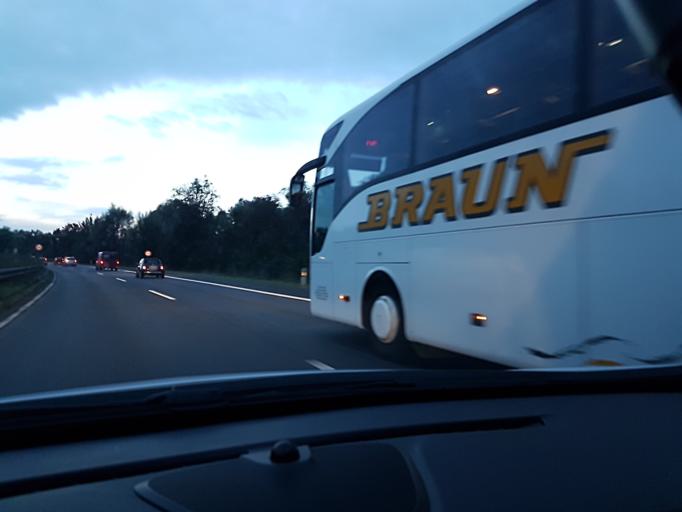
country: DE
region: Hesse
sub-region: Regierungsbezirk Darmstadt
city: Bad Homburg vor der Hoehe
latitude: 50.1741
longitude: 8.6484
